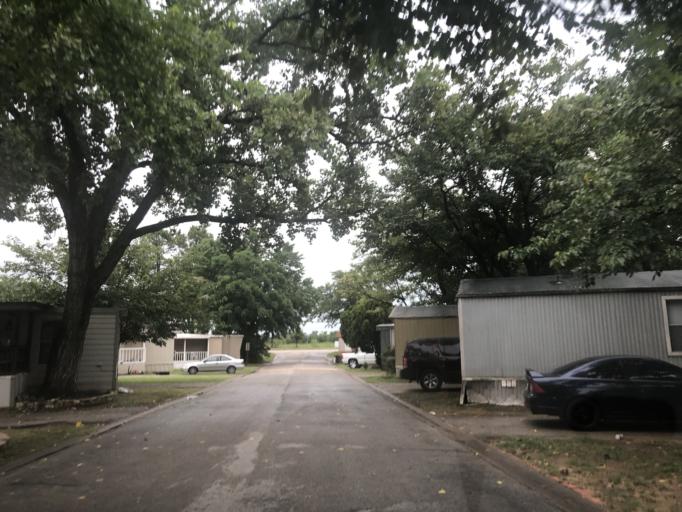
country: US
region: Texas
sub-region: Dallas County
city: Irving
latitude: 32.7839
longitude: -96.9706
